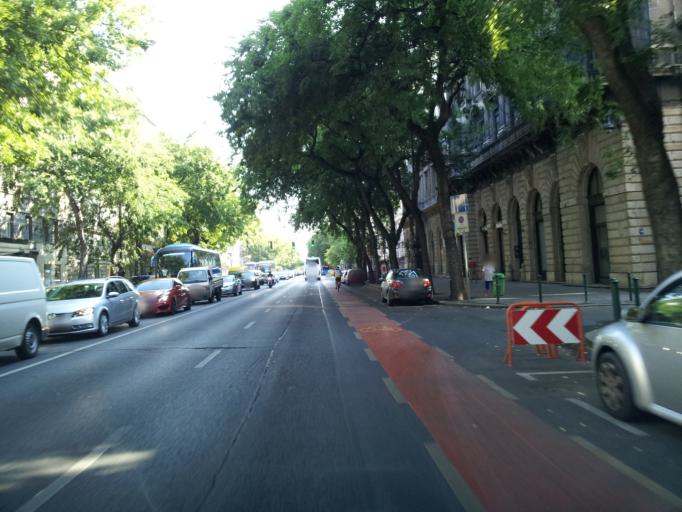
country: HU
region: Budapest
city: Budapest VI. keruelet
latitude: 47.5014
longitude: 19.0579
